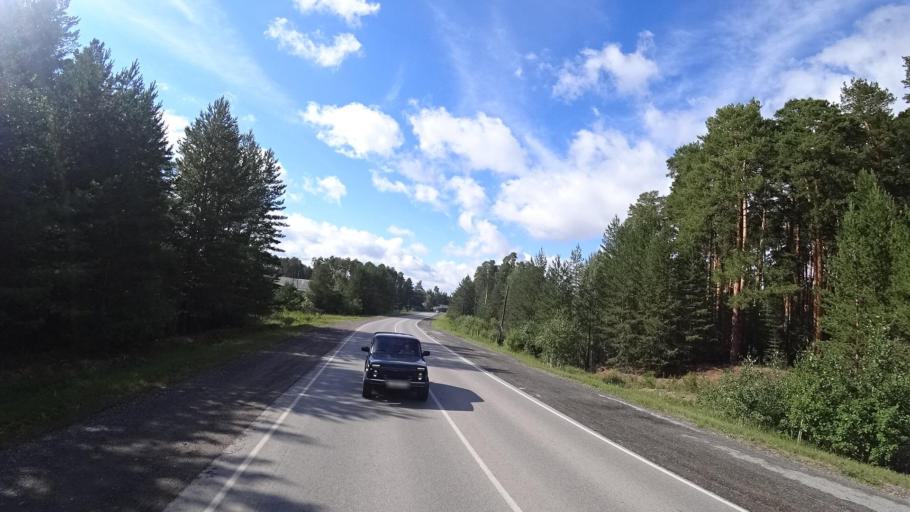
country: RU
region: Sverdlovsk
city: Kamyshlov
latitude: 56.8279
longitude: 62.6975
